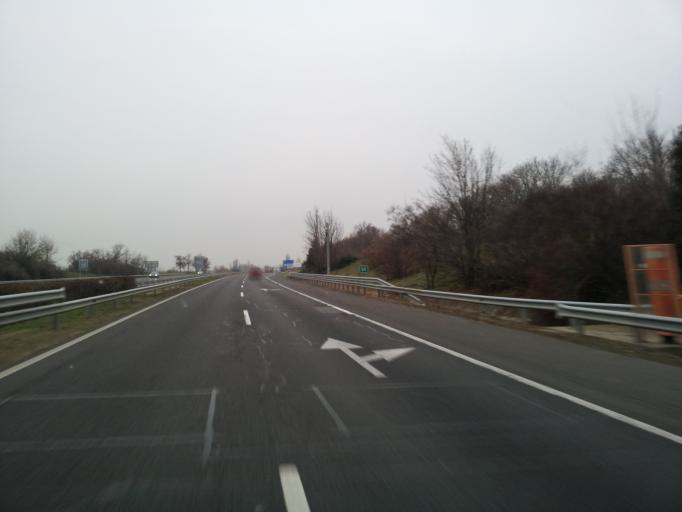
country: HU
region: Fejer
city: Pakozd
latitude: 47.1834
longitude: 18.4924
